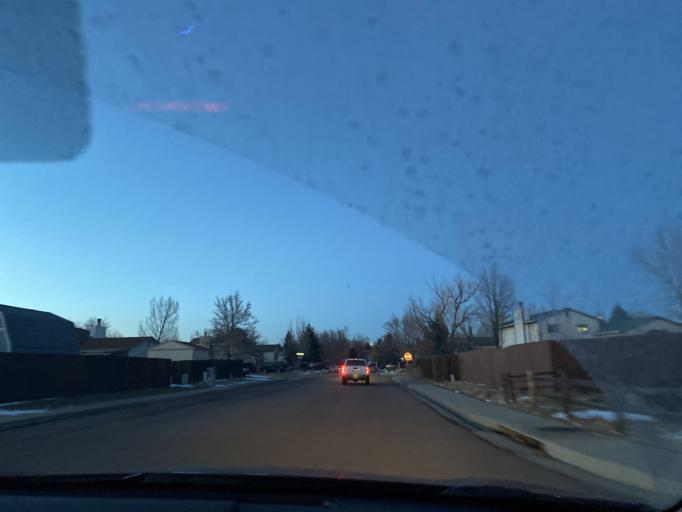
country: US
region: Colorado
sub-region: El Paso County
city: Security-Widefield
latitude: 38.7243
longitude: -104.6903
